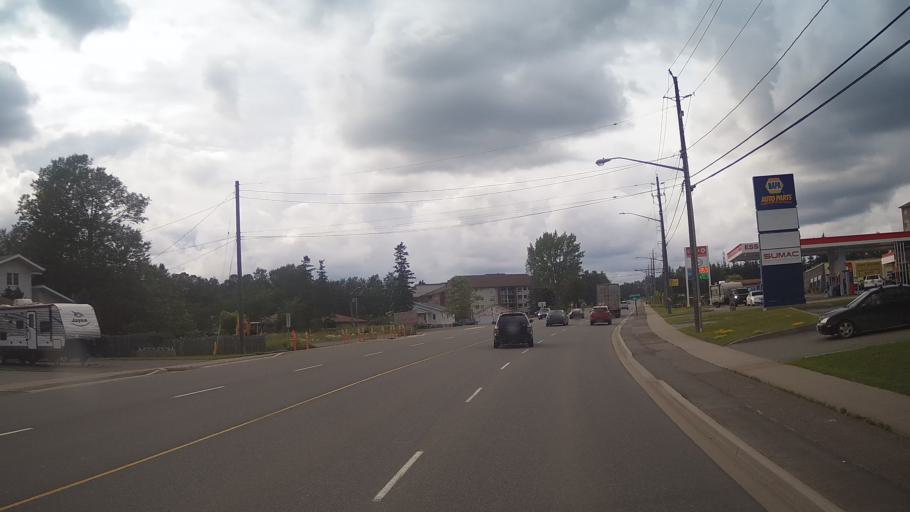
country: CA
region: Ontario
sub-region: Thunder Bay District
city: Thunder Bay
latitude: 48.4550
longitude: -89.2625
